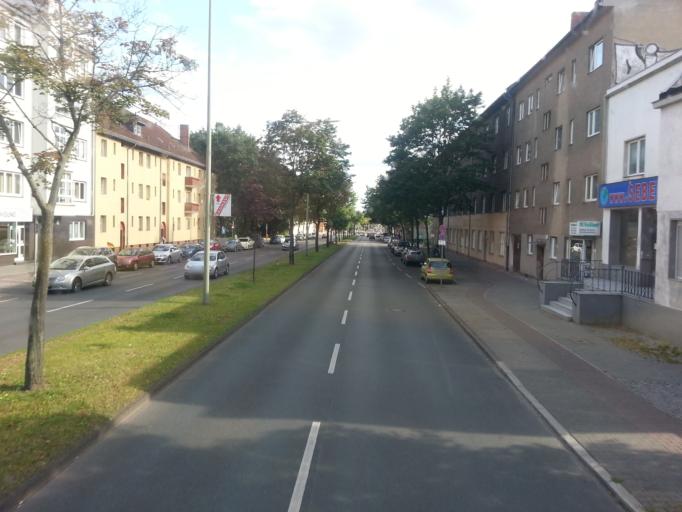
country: DE
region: Berlin
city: Reinickendorf
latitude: 52.5777
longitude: 13.3328
